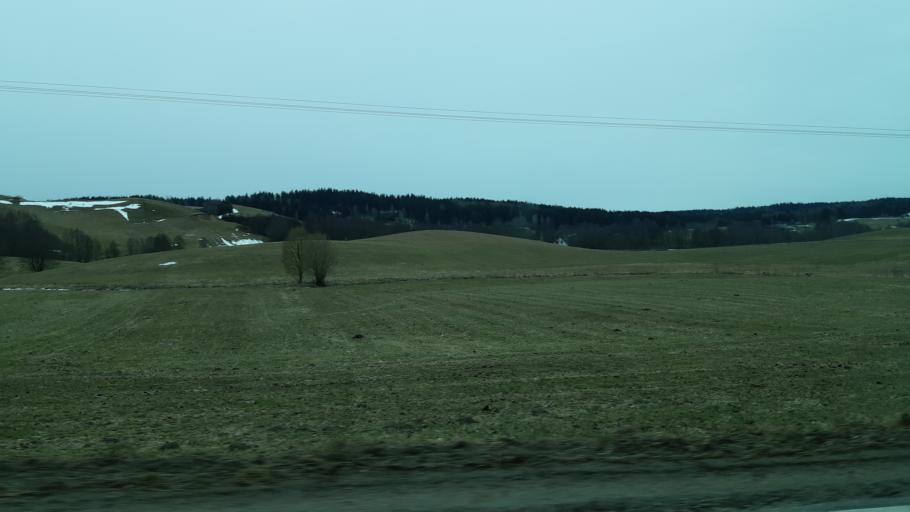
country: PL
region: Podlasie
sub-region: Suwalki
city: Suwalki
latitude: 54.3348
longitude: 22.9315
